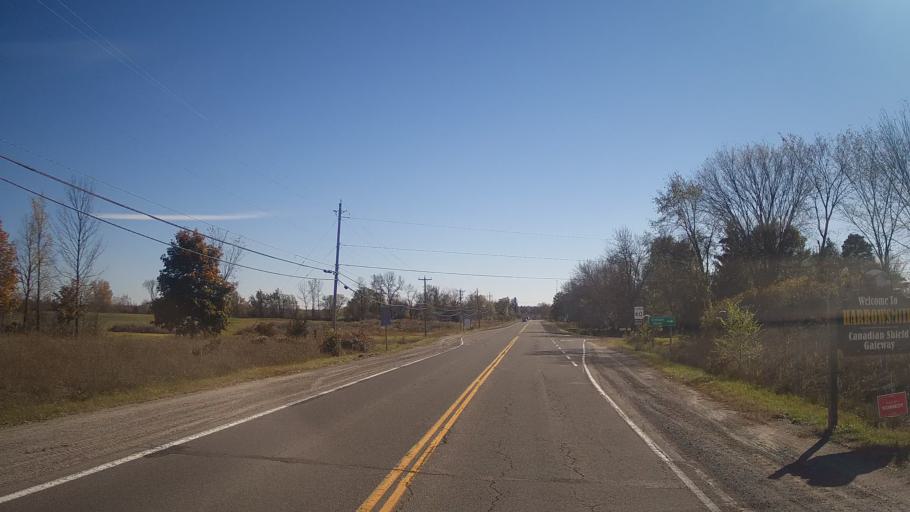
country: CA
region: Ontario
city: Kingston
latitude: 44.4149
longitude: -76.6665
